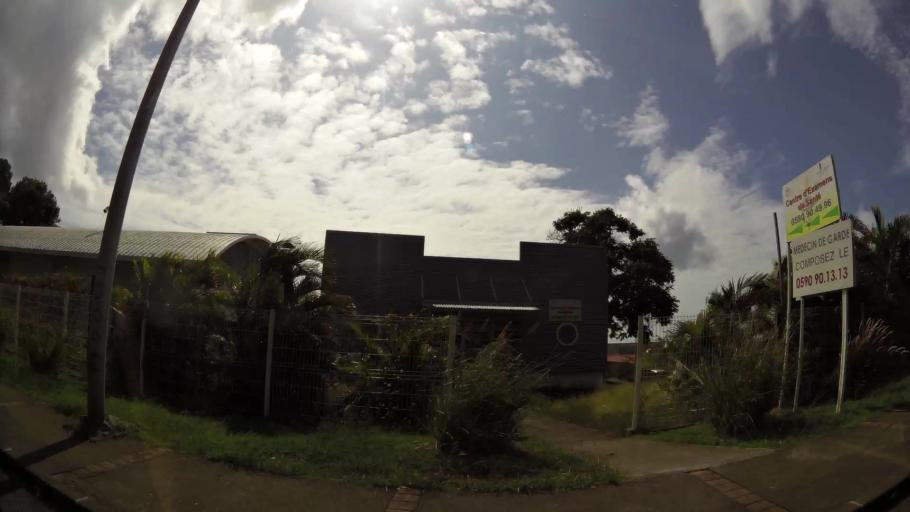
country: GP
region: Guadeloupe
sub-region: Guadeloupe
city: Basse-Terre
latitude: 16.0038
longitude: -61.7285
